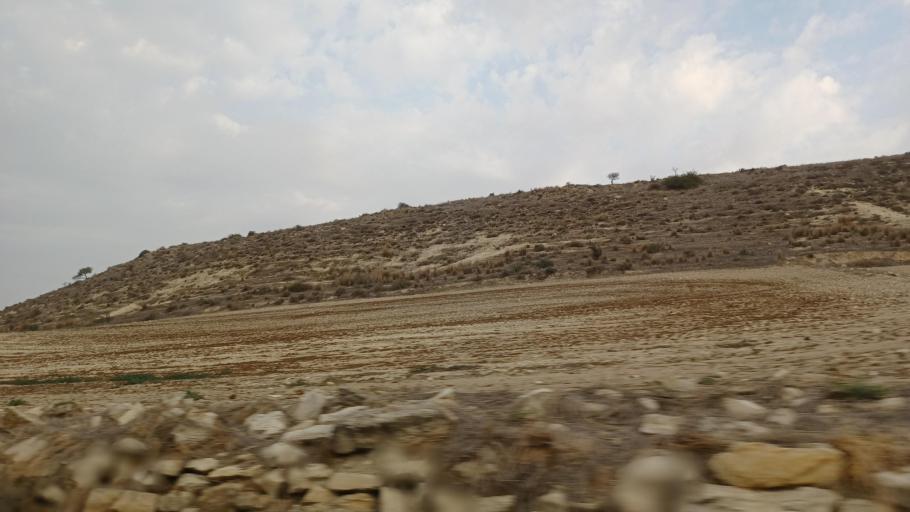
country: CY
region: Larnaka
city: Athienou
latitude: 35.0379
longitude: 33.5595
